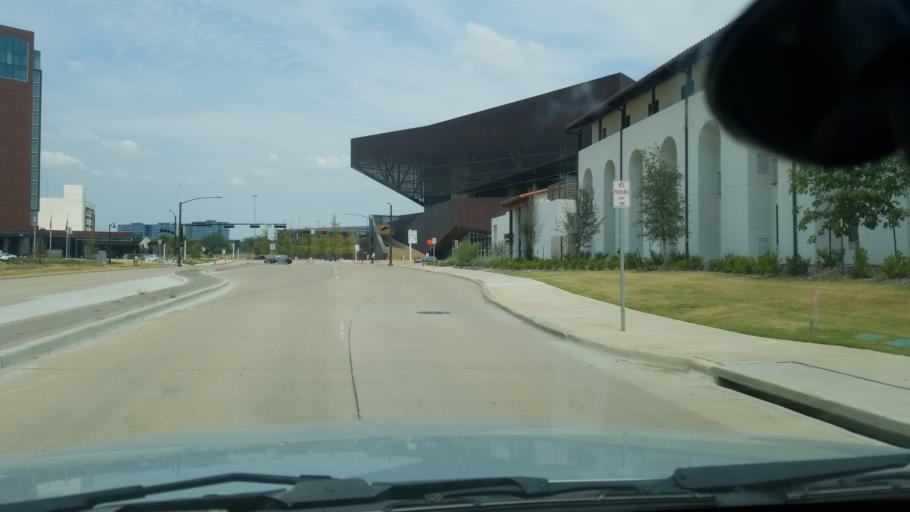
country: US
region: Texas
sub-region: Dallas County
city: Irving
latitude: 32.8767
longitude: -96.9414
